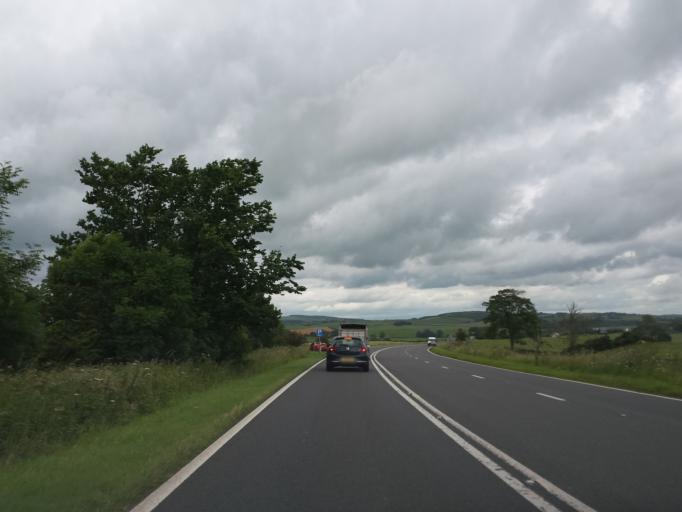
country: GB
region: Scotland
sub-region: Dumfries and Galloway
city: Castle Douglas
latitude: 54.9689
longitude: -3.9025
